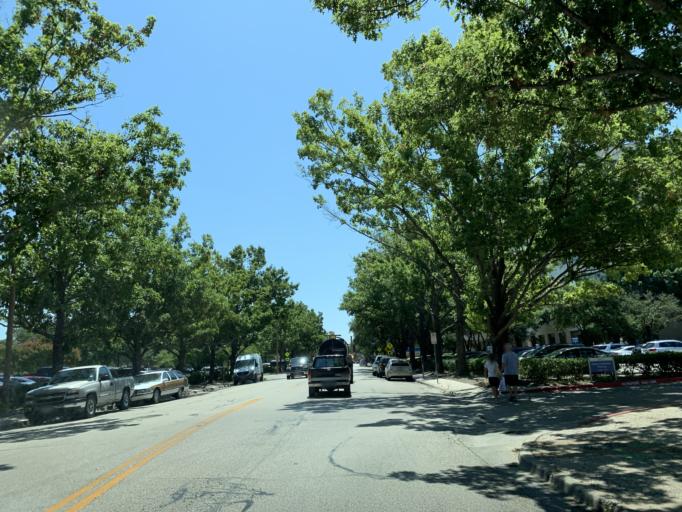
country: US
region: Texas
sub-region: Dallas County
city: Dallas
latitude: 32.7898
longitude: -96.7768
